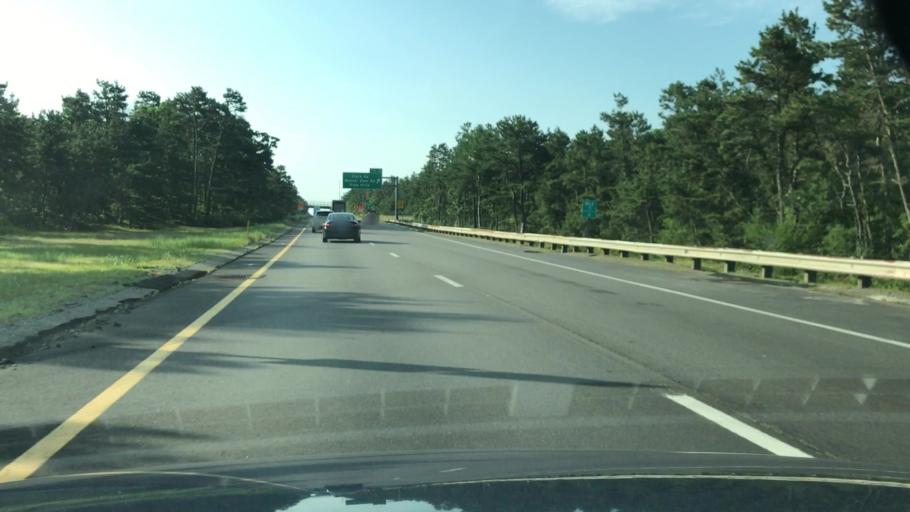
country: US
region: Massachusetts
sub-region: Plymouth County
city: White Island Shores
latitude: 41.8770
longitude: -70.6055
